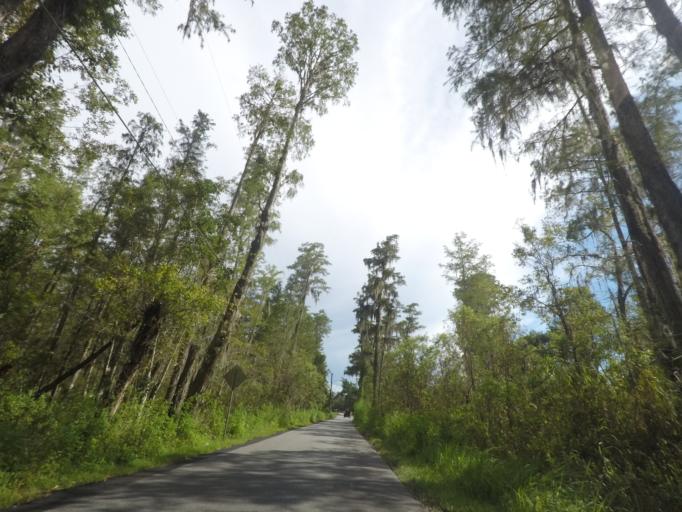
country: US
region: Florida
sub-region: Osceola County
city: Kissimmee
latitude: 28.3191
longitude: -81.4626
